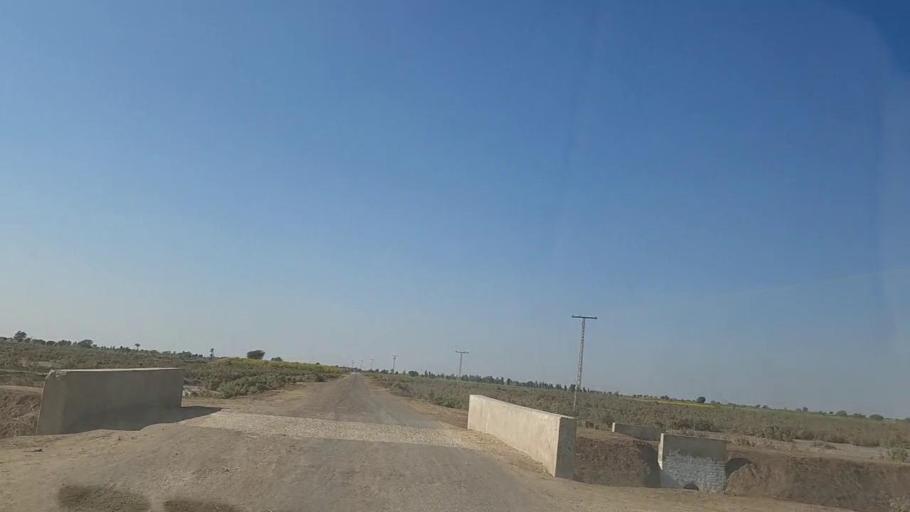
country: PK
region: Sindh
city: Digri
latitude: 25.1685
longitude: 69.0217
